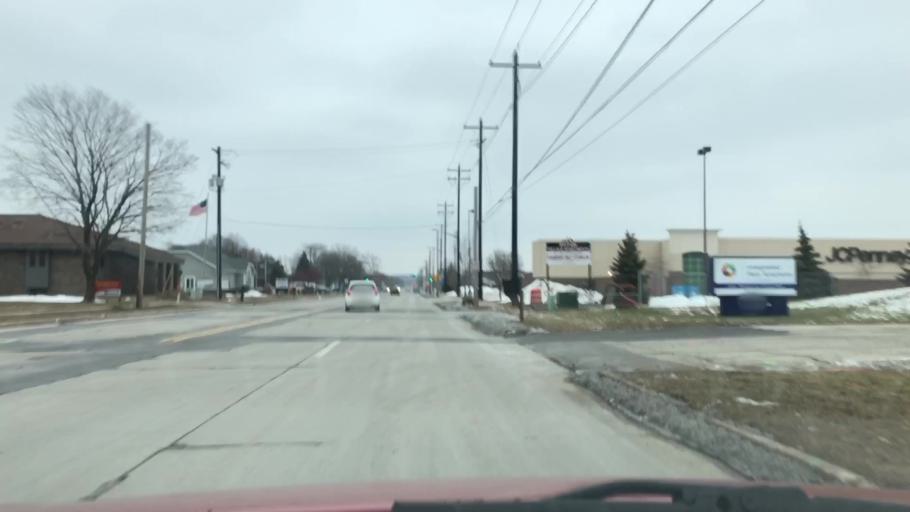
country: US
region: Wisconsin
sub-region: Brown County
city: Ashwaubenon
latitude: 44.4888
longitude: -88.0635
